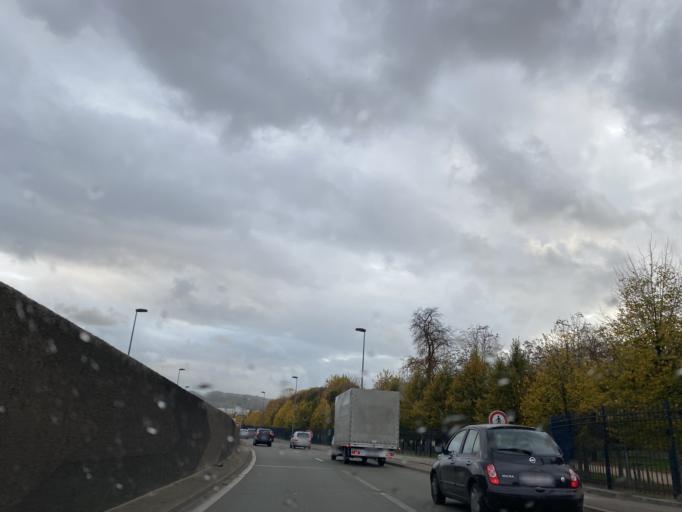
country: FR
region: Ile-de-France
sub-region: Departement des Hauts-de-Seine
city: Sevres
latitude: 48.8393
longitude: 2.2212
